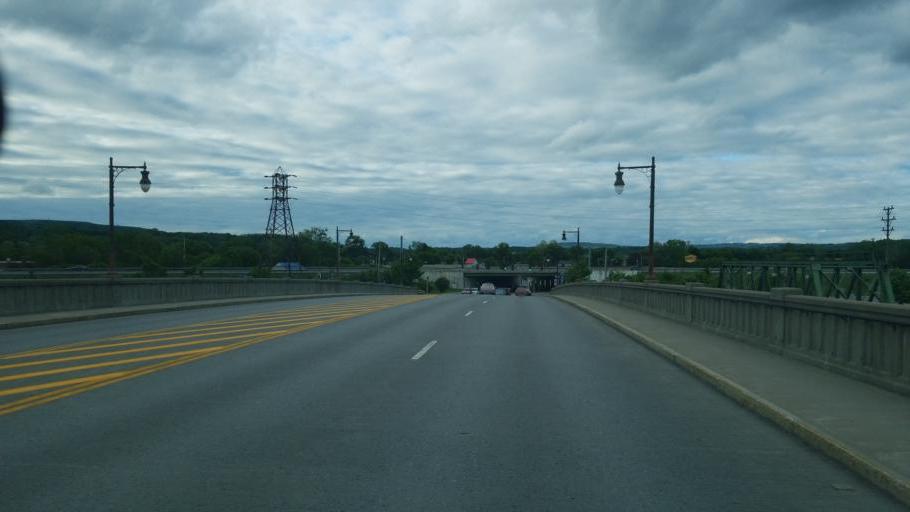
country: US
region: New York
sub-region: Herkimer County
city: Mohawk
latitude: 43.0158
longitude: -74.9946
